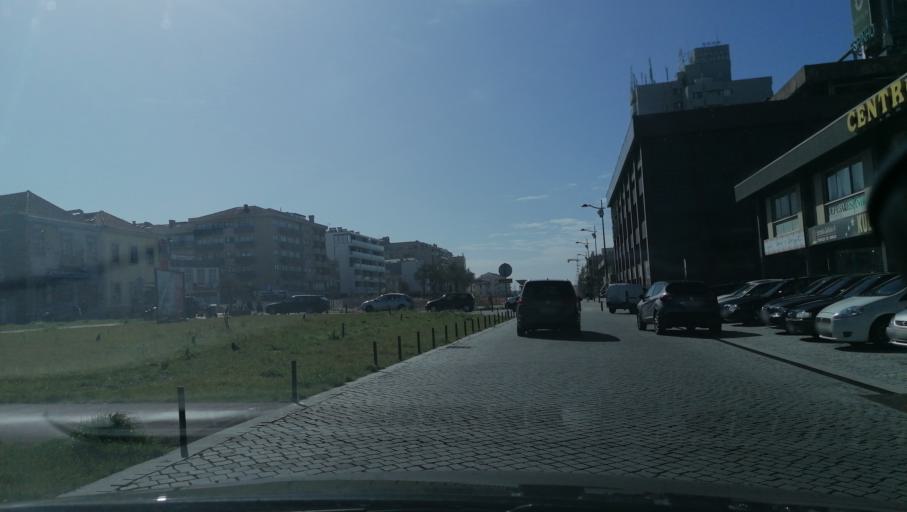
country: PT
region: Aveiro
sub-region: Espinho
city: Espinho
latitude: 41.0095
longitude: -8.6444
